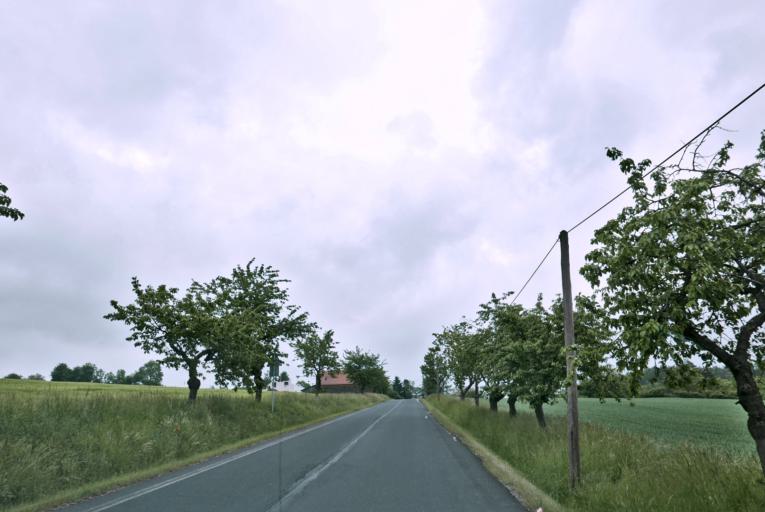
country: CZ
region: Plzensky
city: Plasy
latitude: 49.9814
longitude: 13.3971
